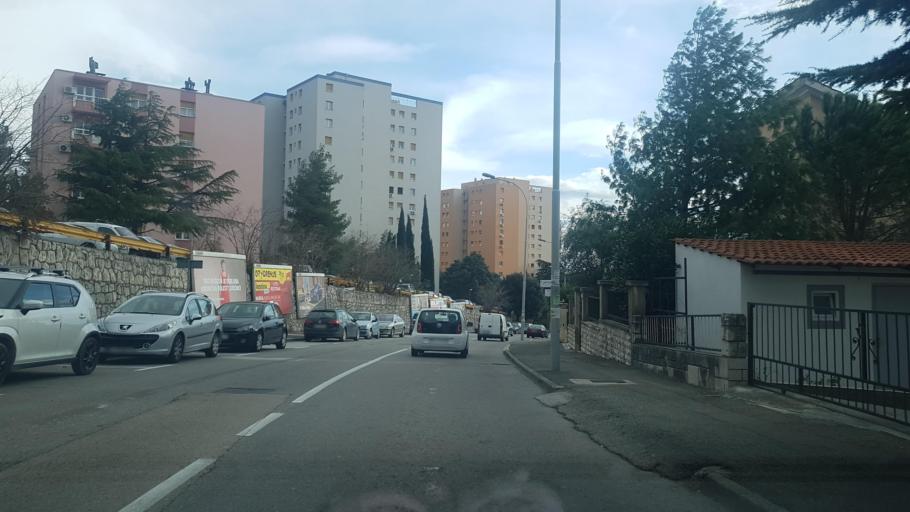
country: HR
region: Primorsko-Goranska
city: Cavle
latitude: 45.3218
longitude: 14.4784
